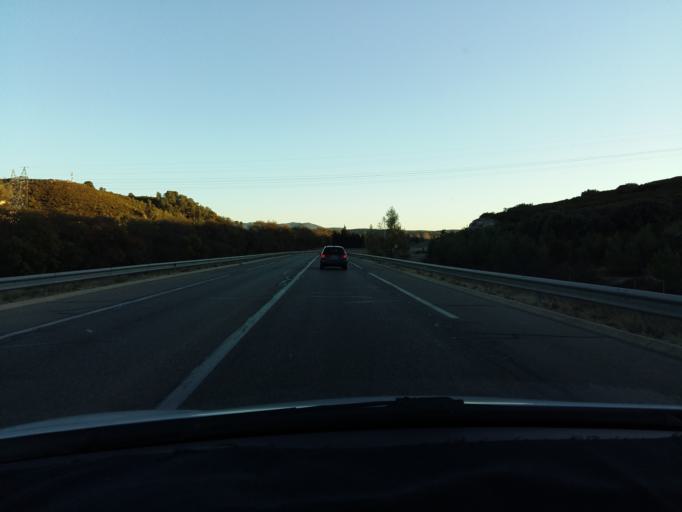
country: FR
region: Provence-Alpes-Cote d'Azur
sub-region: Departement des Bouches-du-Rhone
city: Cabries
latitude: 43.4861
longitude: 5.3529
